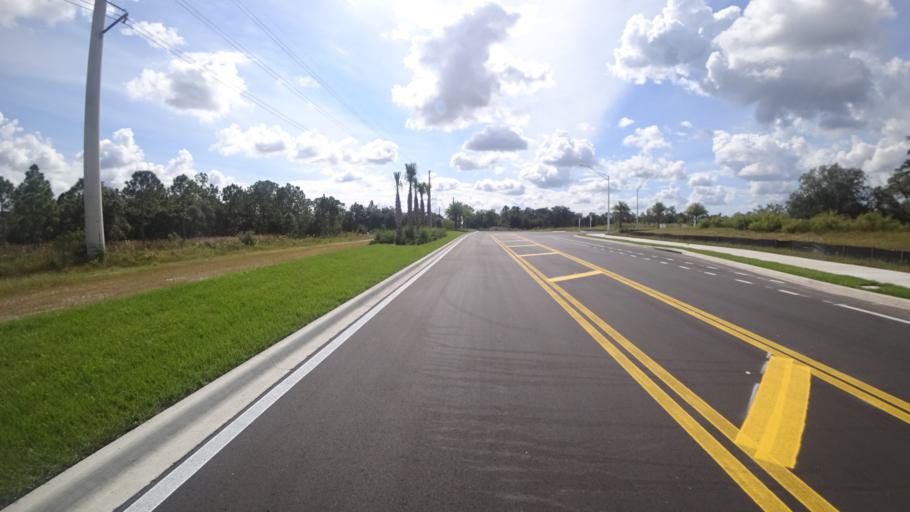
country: US
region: Florida
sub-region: Sarasota County
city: The Meadows
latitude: 27.4034
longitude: -82.3543
